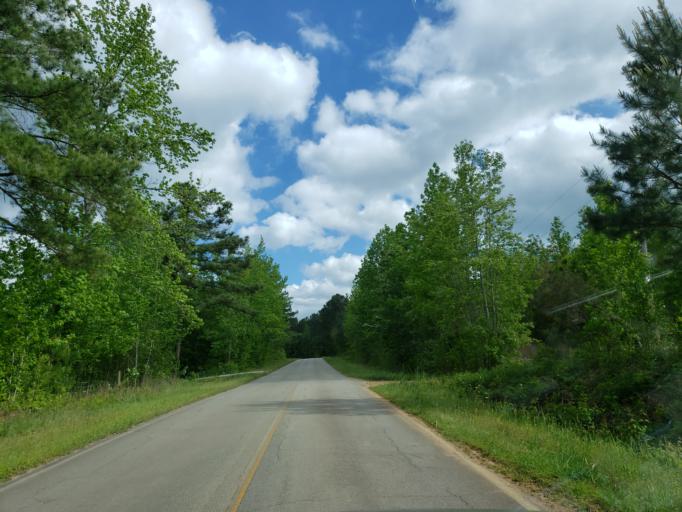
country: US
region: Georgia
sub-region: Haralson County
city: Tallapoosa
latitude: 33.6881
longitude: -85.3224
